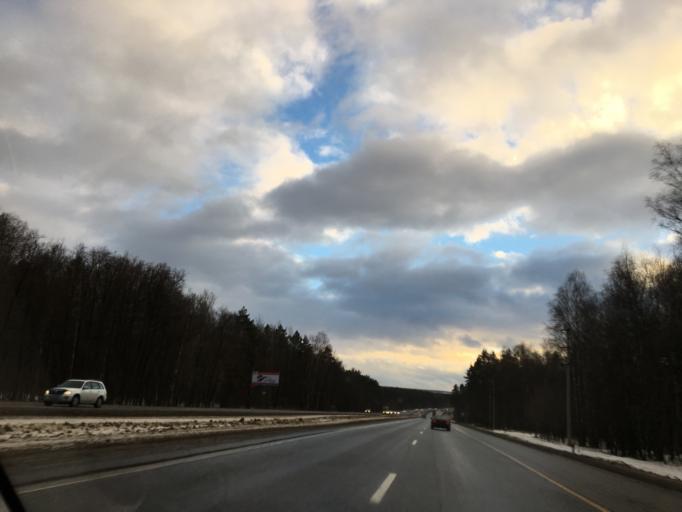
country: RU
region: Moskovskaya
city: Danki
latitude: 54.8917
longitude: 37.5117
